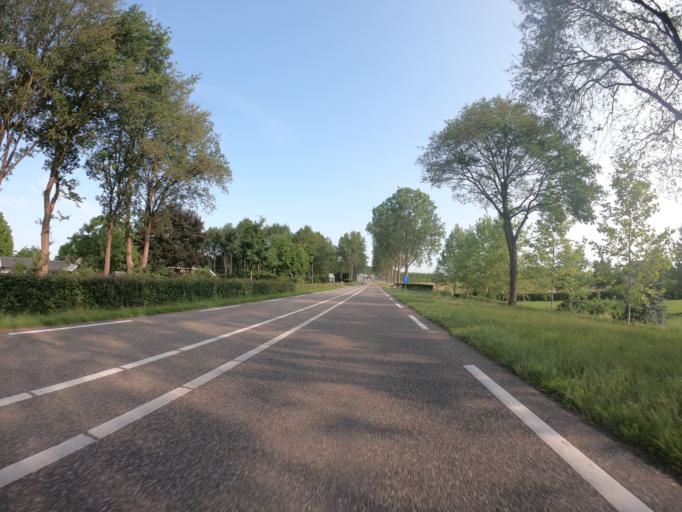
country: NL
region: North Brabant
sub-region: Gemeente Landerd
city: Reek
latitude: 51.7391
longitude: 5.6696
